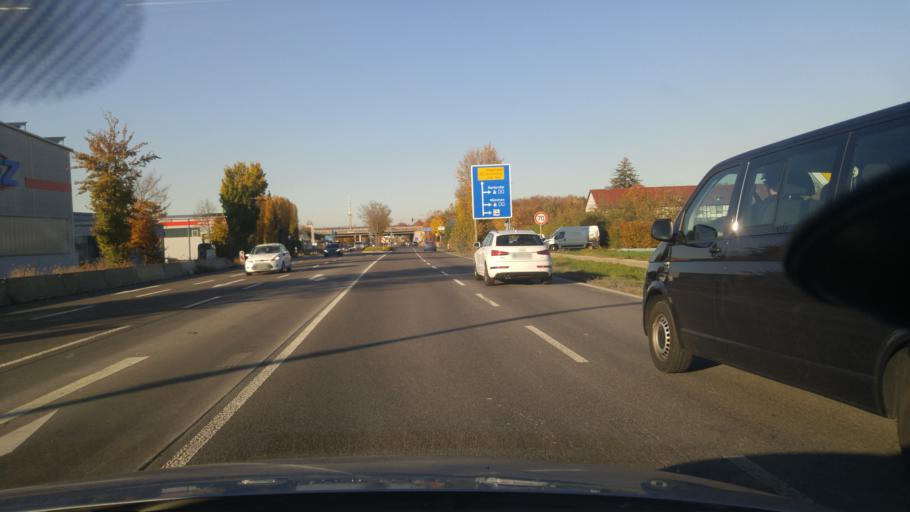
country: DE
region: Baden-Wuerttemberg
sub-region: Regierungsbezirk Stuttgart
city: Dettingen unter Teck
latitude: 48.6278
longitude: 9.4556
